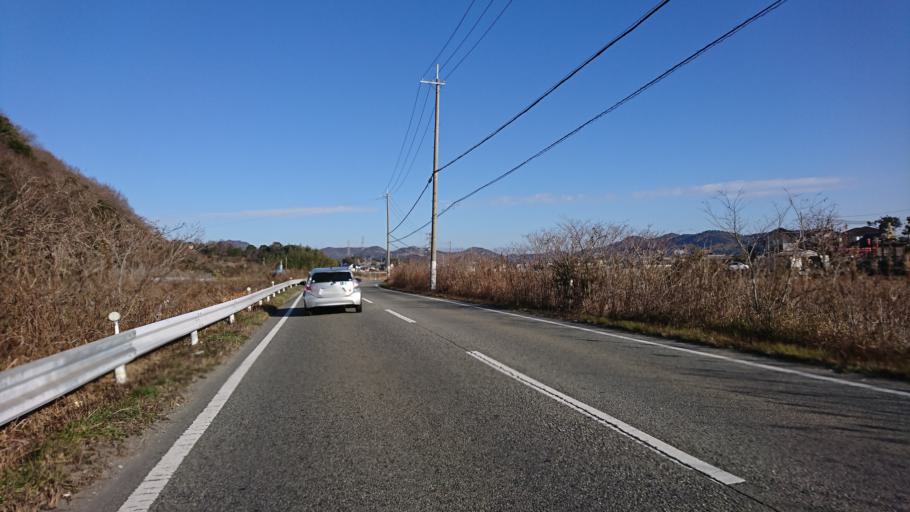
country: JP
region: Hyogo
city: Kakogawacho-honmachi
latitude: 34.7910
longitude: 134.8624
